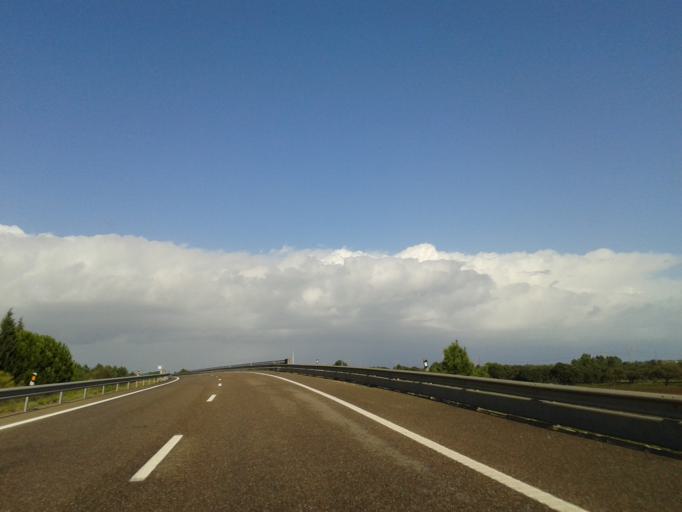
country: PT
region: Setubal
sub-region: Palmela
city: Palmela
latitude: 38.5861
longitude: -8.8630
